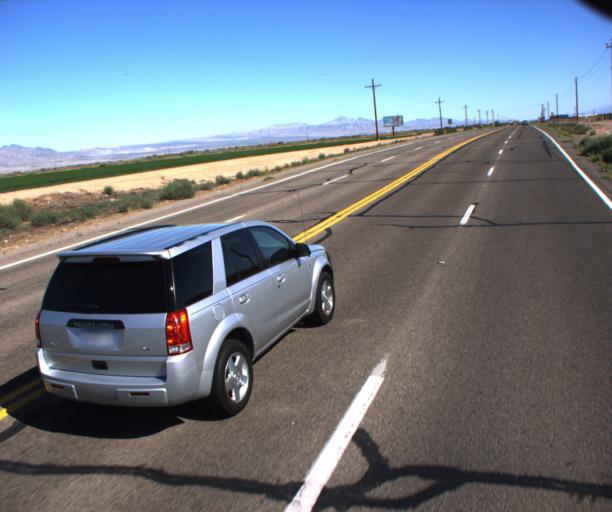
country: US
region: Arizona
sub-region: Mohave County
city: Mohave Valley
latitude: 34.9342
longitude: -114.5978
